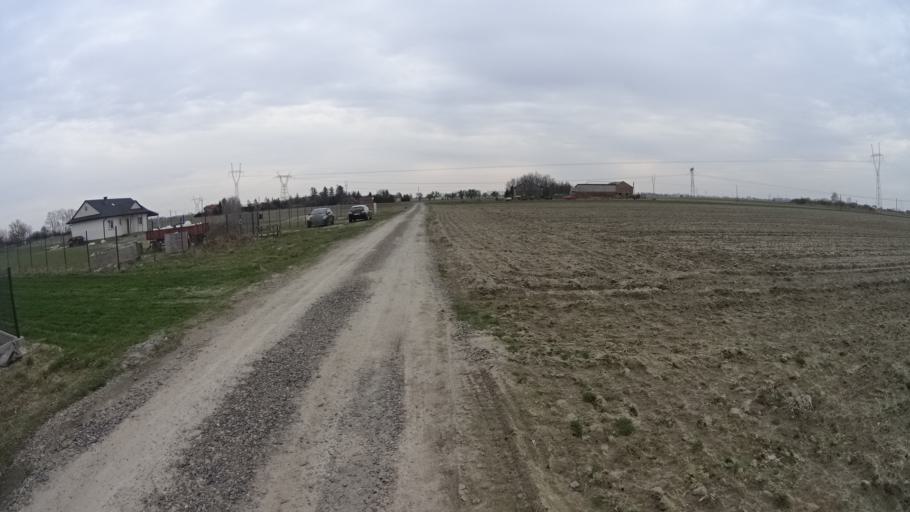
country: PL
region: Masovian Voivodeship
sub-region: Powiat warszawski zachodni
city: Jozefow
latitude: 52.2414
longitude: 20.6888
